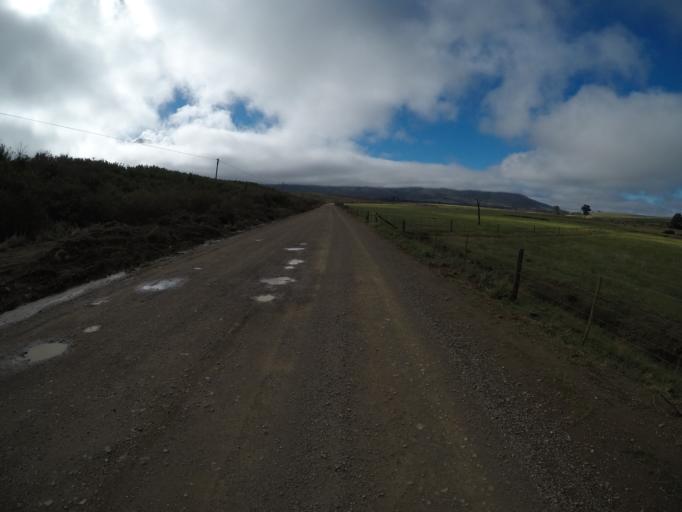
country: ZA
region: Western Cape
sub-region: Cape Winelands District Municipality
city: Ashton
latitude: -34.1262
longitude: 19.8231
